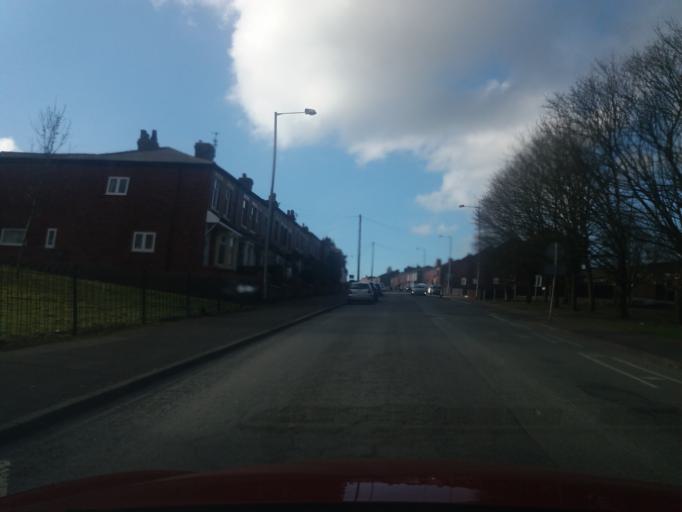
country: GB
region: England
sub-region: Lancashire
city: Chorley
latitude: 53.6484
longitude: -2.6143
